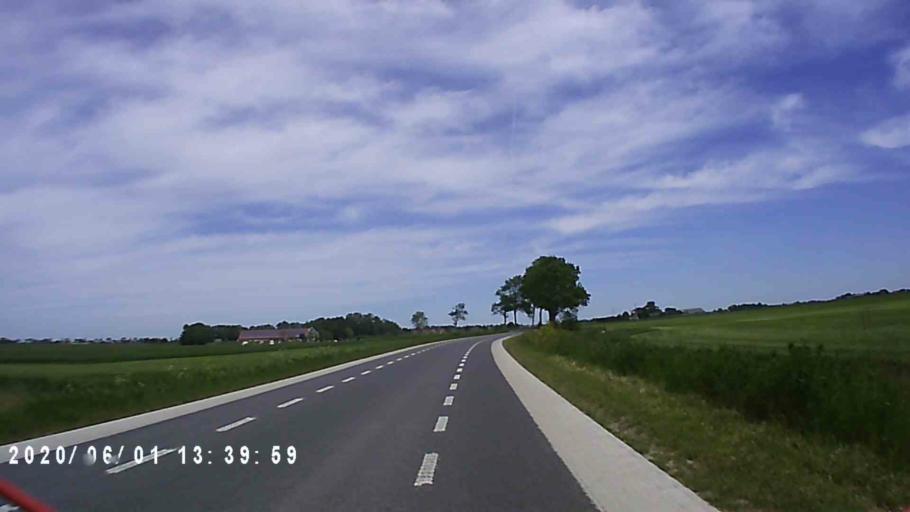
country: NL
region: Friesland
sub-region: Gemeente Littenseradiel
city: Wommels
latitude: 53.0881
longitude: 5.6017
